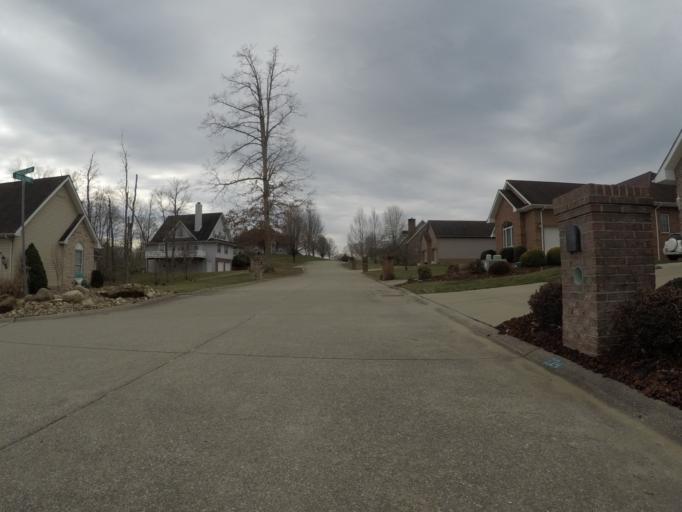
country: US
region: West Virginia
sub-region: Cabell County
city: Pea Ridge
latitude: 38.3975
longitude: -82.3777
